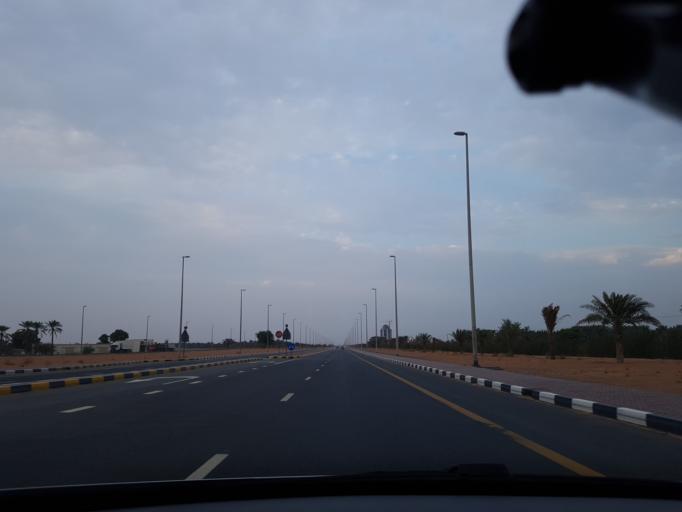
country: AE
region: Ash Shariqah
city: Adh Dhayd
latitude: 25.2722
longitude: 55.9121
